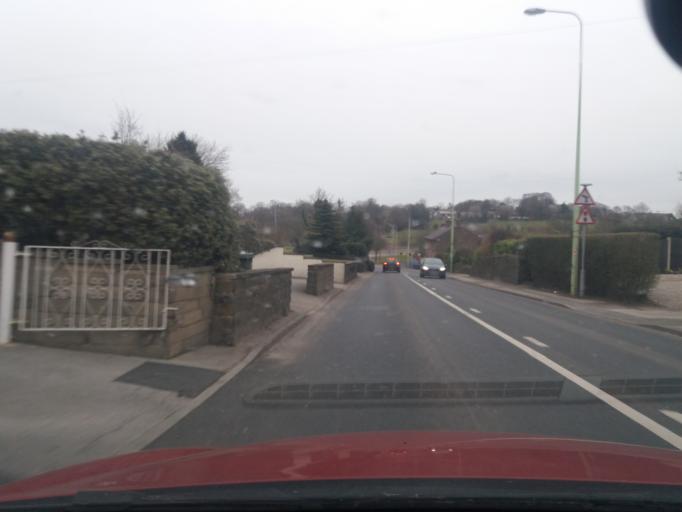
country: GB
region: England
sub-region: Lancashire
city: Chorley
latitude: 53.6778
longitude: -2.6162
